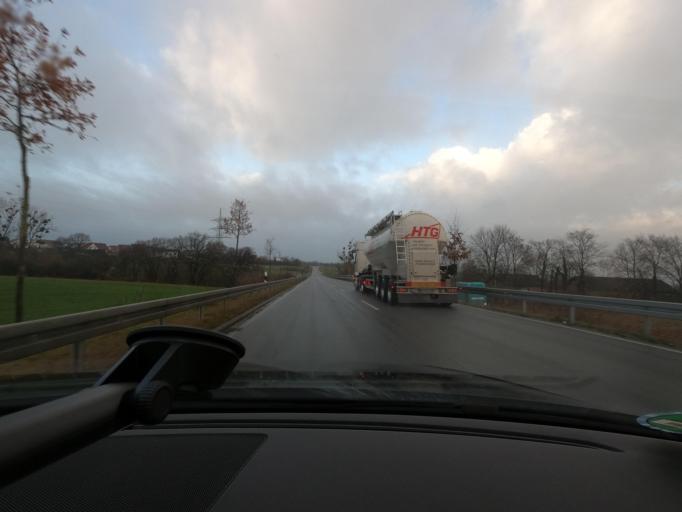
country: DE
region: North Rhine-Westphalia
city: Geseke
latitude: 51.5912
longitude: 8.5215
